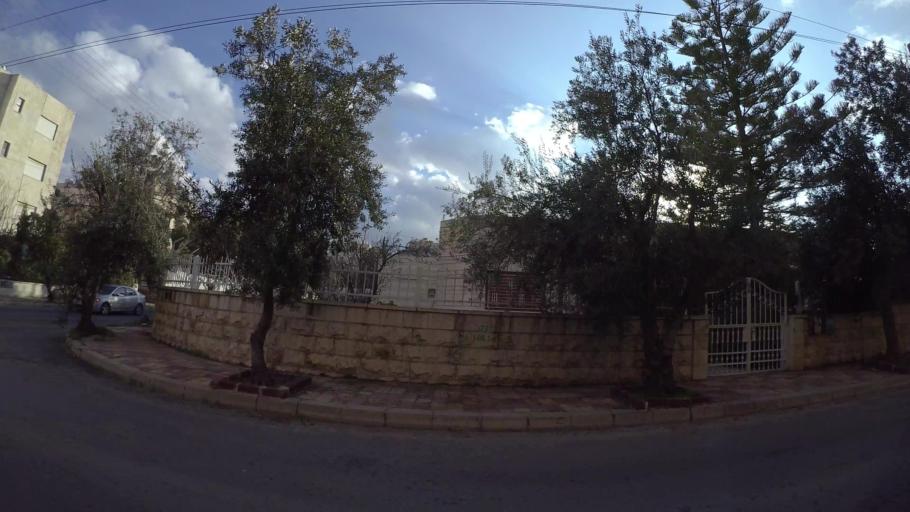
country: JO
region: Amman
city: Al Jubayhah
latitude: 31.9818
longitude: 35.8913
